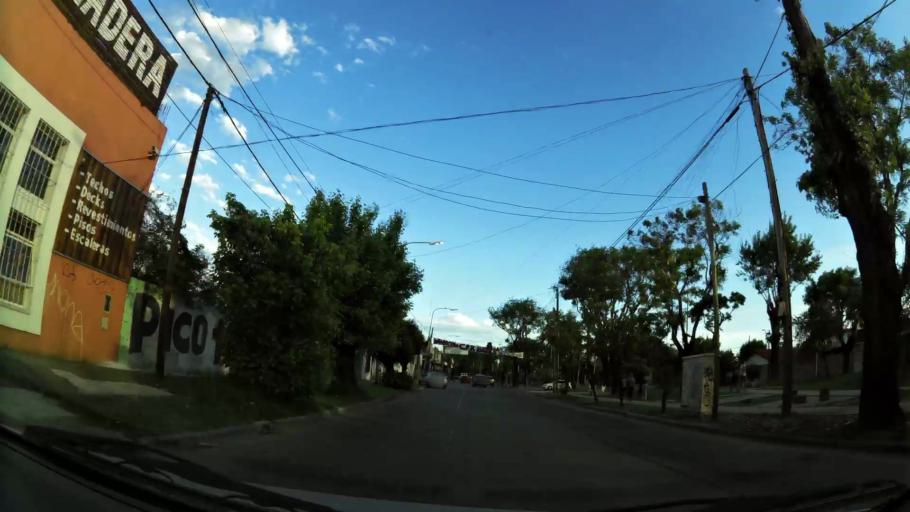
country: AR
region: Buenos Aires
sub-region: Partido de Avellaneda
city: Avellaneda
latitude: -34.7014
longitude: -58.3409
